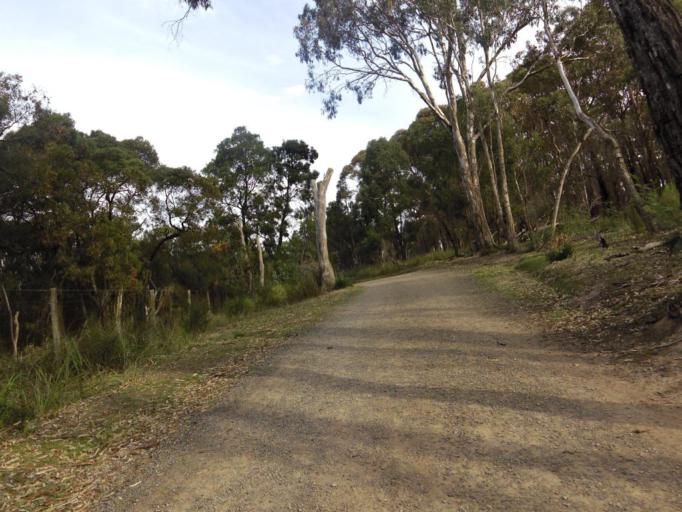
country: AU
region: Victoria
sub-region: Yarra Ranges
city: Lysterfield
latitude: -37.9560
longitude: 145.2948
